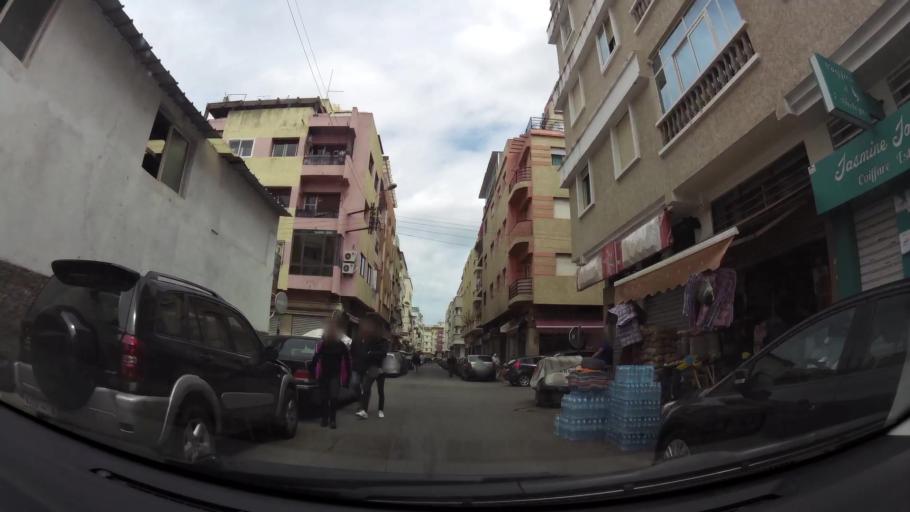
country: MA
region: Grand Casablanca
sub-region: Casablanca
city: Casablanca
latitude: 33.5722
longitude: -7.6440
